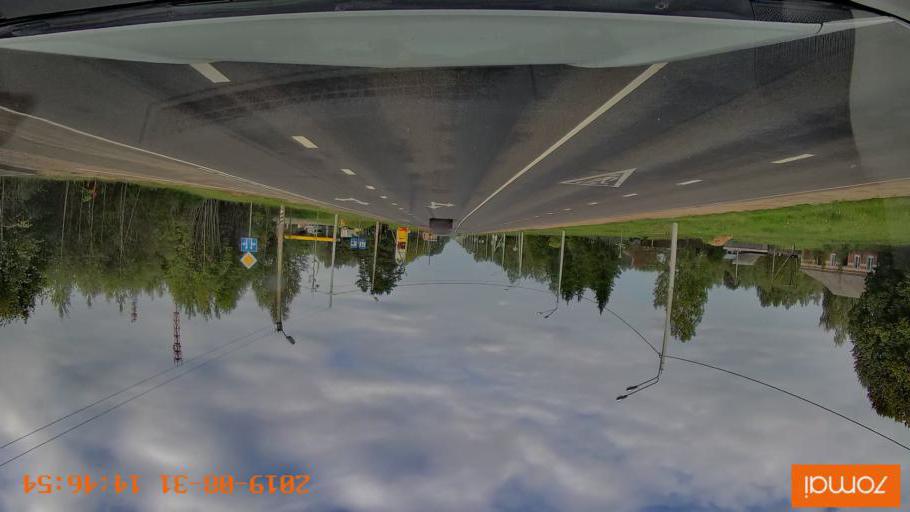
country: RU
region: Kaluga
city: Betlitsa
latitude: 54.2365
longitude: 33.7181
